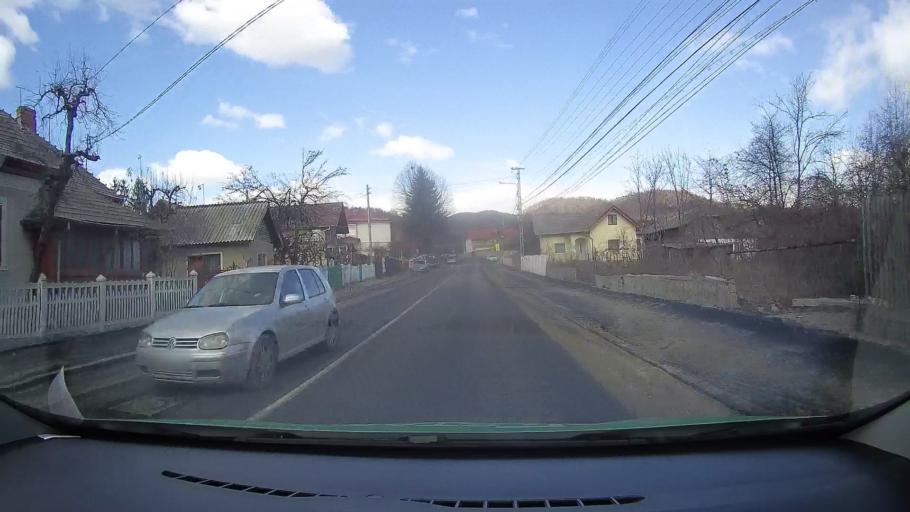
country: RO
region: Dambovita
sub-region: Comuna Fieni
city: Fieni
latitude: 45.1275
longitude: 25.4184
